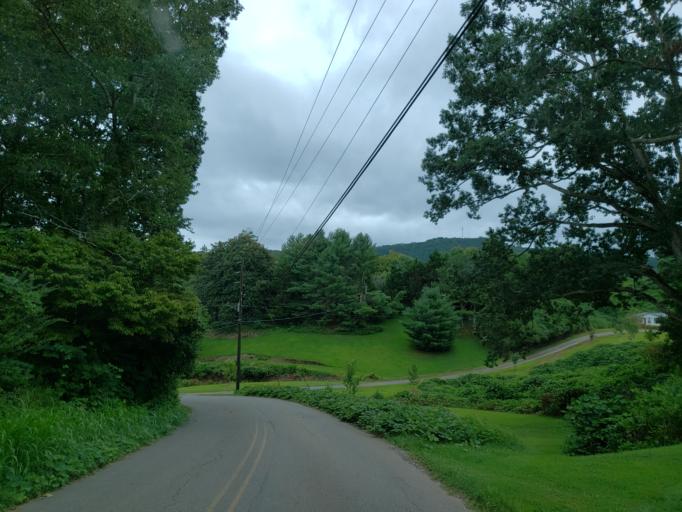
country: US
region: Georgia
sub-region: Gilmer County
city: Ellijay
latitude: 34.6422
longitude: -84.5012
